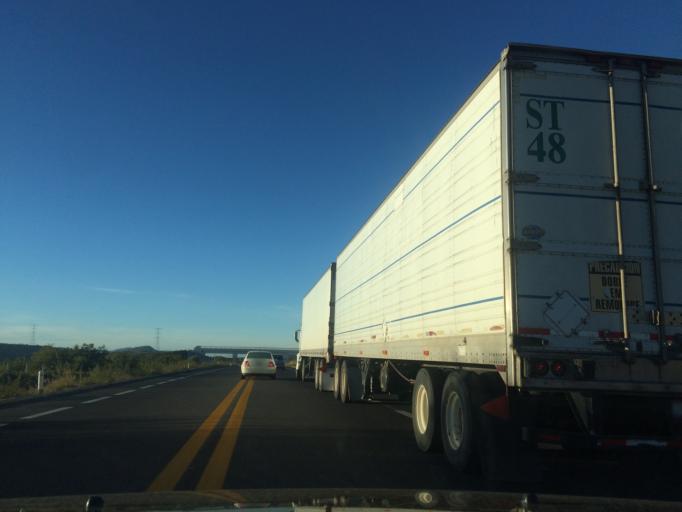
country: MX
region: Puebla
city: Morelos Canada
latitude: 18.7128
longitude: -97.4699
